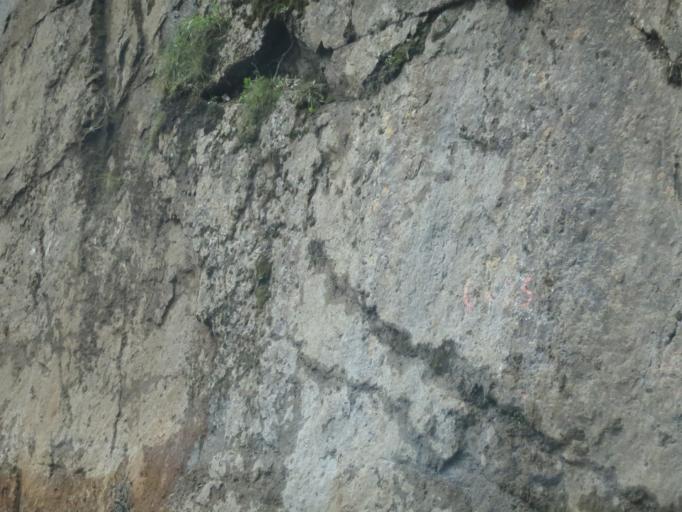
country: GE
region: Kakheti
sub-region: Telavi
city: Telavi
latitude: 42.2271
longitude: 45.4806
